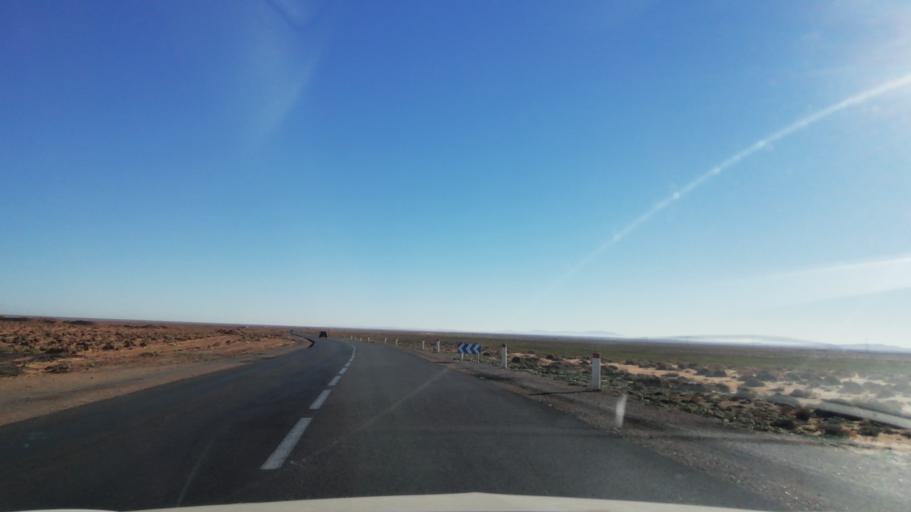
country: DZ
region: El Bayadh
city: El Bayadh
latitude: 33.8592
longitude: 0.5460
